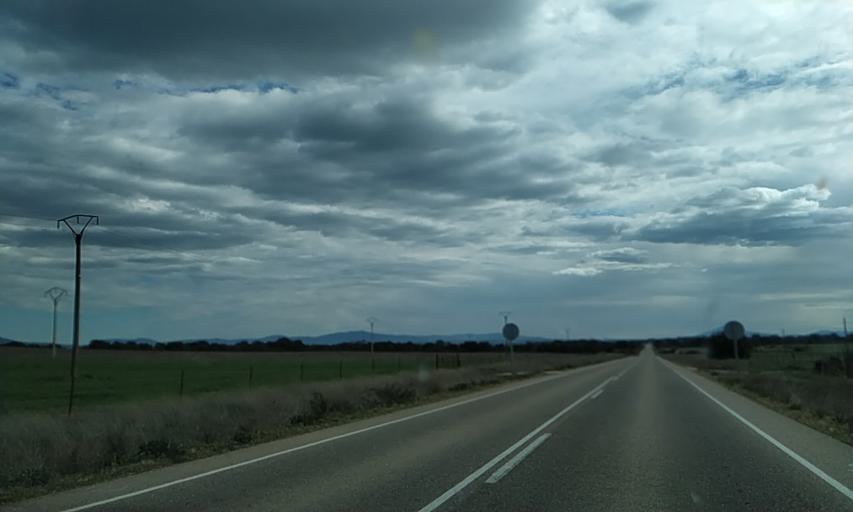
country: ES
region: Castille and Leon
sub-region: Provincia de Salamanca
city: Herguijuela de Ciudad Rodrigo
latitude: 40.4730
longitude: -6.5810
